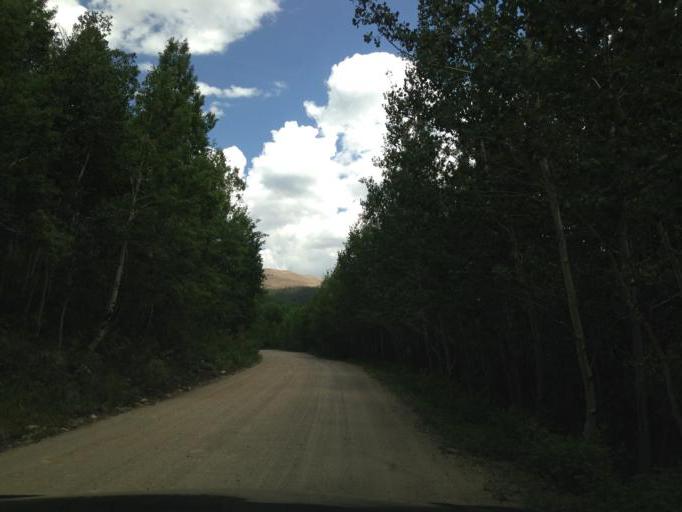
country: US
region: Colorado
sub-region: Park County
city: Fairplay
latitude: 39.3446
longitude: -105.9204
